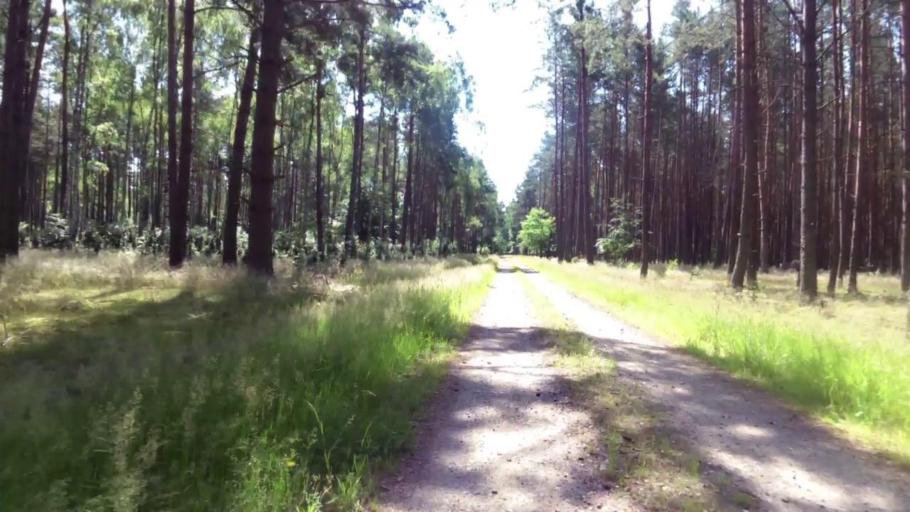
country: PL
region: West Pomeranian Voivodeship
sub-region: Powiat swidwinski
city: Polczyn-Zdroj
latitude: 53.8565
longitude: 16.1331
